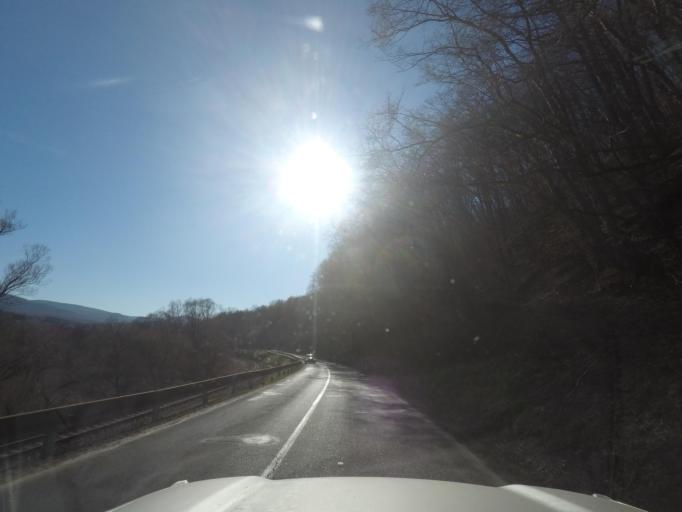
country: SK
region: Presovsky
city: Snina
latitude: 48.9873
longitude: 22.2025
